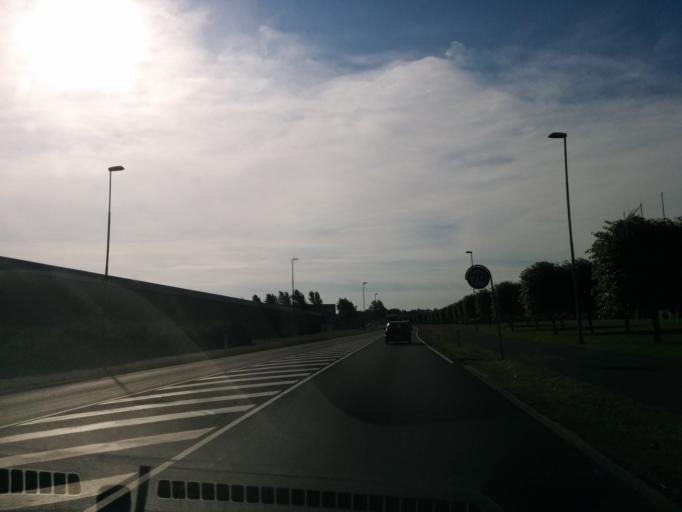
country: DK
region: Central Jutland
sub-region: Arhus Kommune
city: Stavtrup
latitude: 56.1111
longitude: 10.1597
